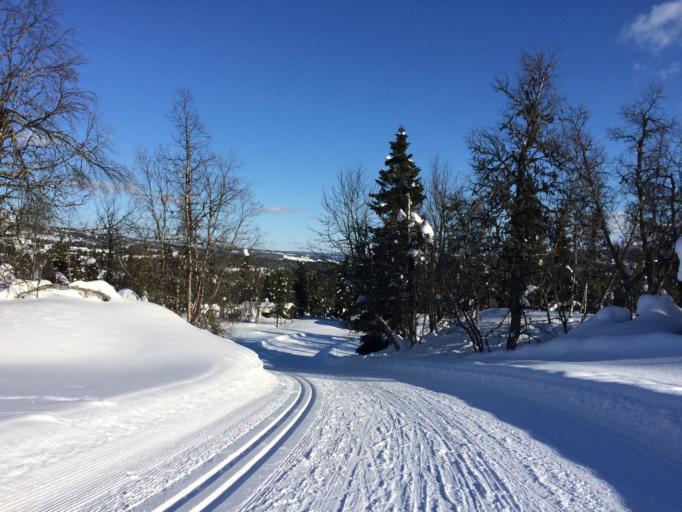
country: NO
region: Oppland
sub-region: Gausdal
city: Segalstad bru
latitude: 61.3347
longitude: 10.0556
